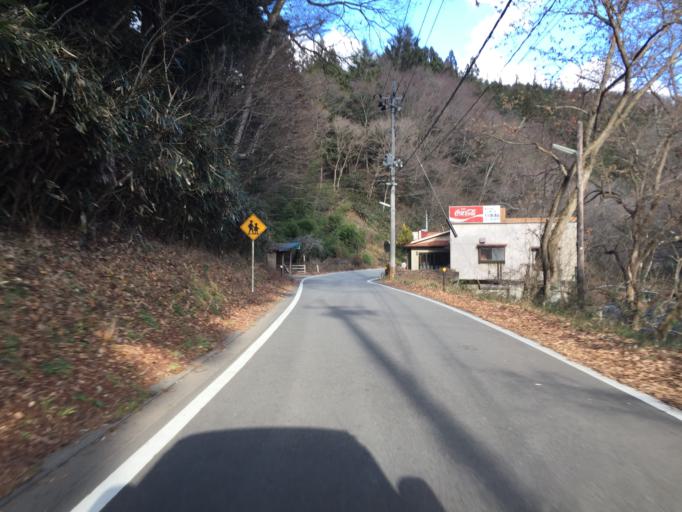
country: JP
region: Fukushima
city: Funehikimachi-funehiki
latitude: 37.2347
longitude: 140.6942
